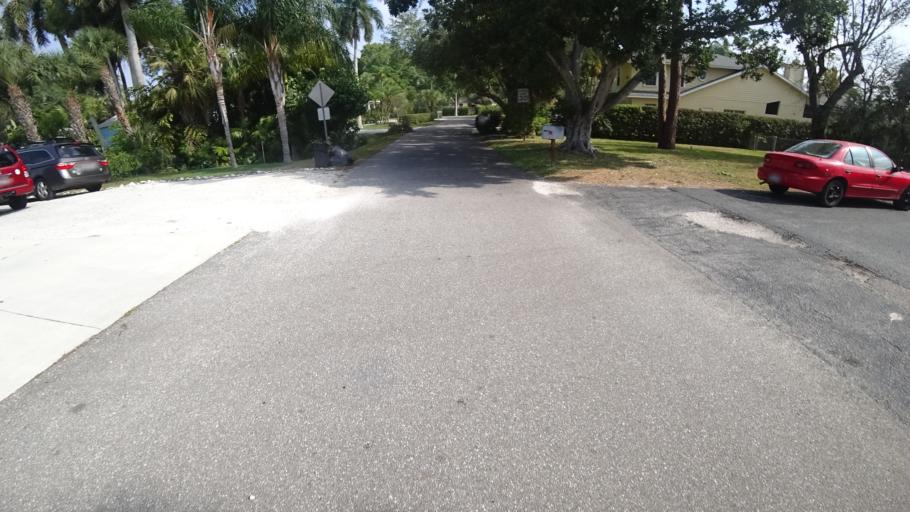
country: US
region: Florida
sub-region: Manatee County
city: West Bradenton
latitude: 27.4996
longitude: -82.6016
